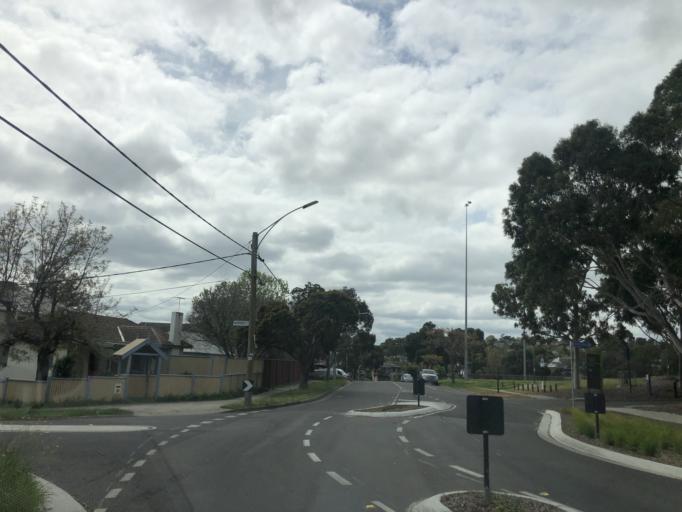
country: AU
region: Victoria
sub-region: Monash
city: Ashwood
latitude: -37.8758
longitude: 145.0986
